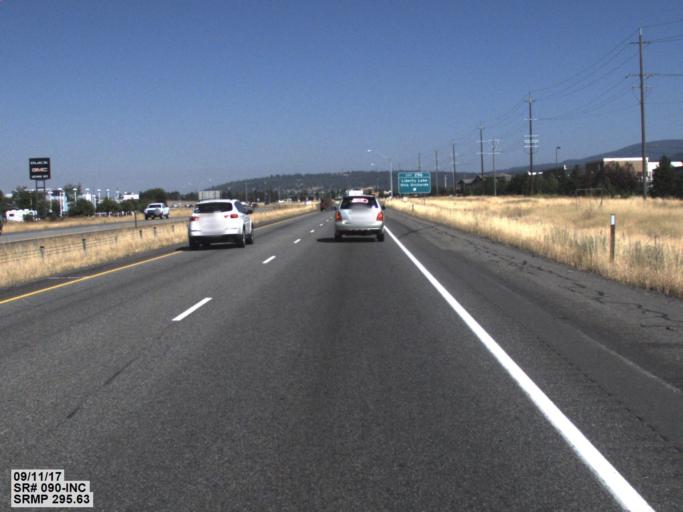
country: US
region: Washington
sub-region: Spokane County
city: Liberty Lake
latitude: 47.6682
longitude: -117.1184
